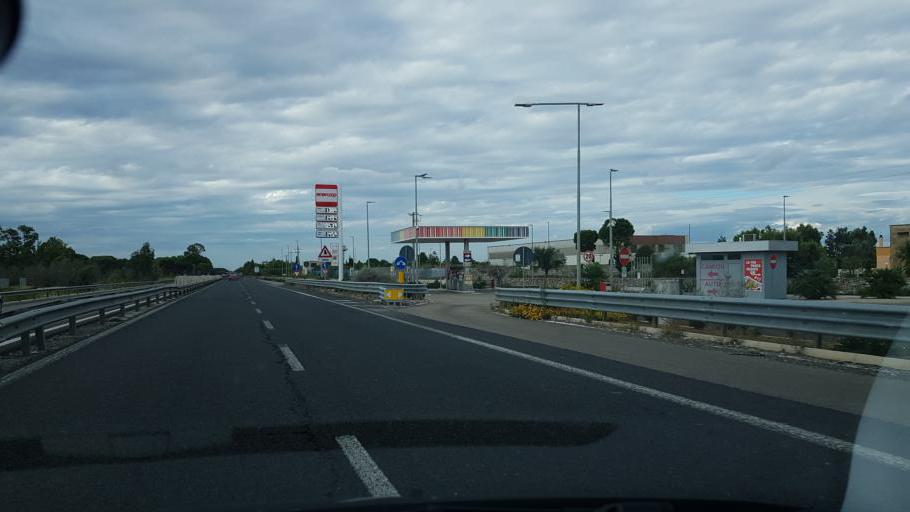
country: IT
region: Apulia
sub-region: Provincia di Lecce
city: San Donato di Lecce
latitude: 40.2804
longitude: 18.2020
